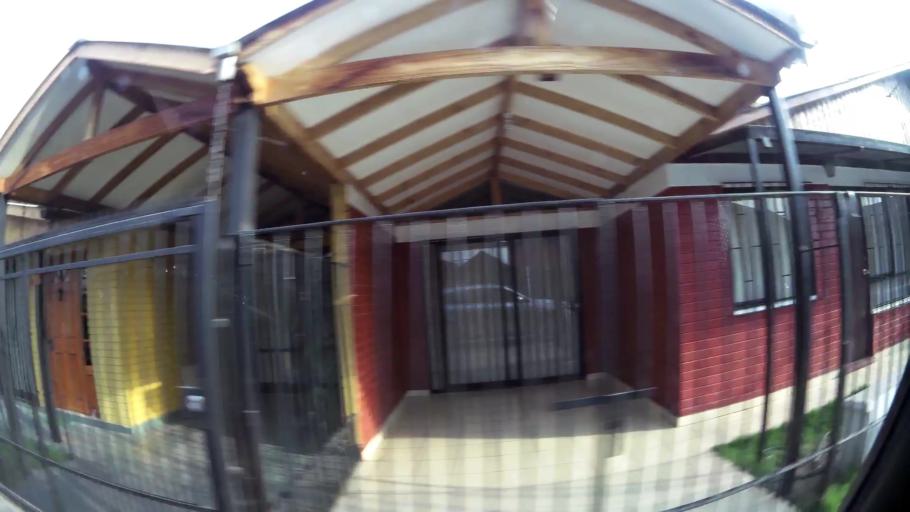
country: CL
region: Santiago Metropolitan
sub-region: Provincia de Maipo
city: San Bernardo
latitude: -33.5319
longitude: -70.7679
